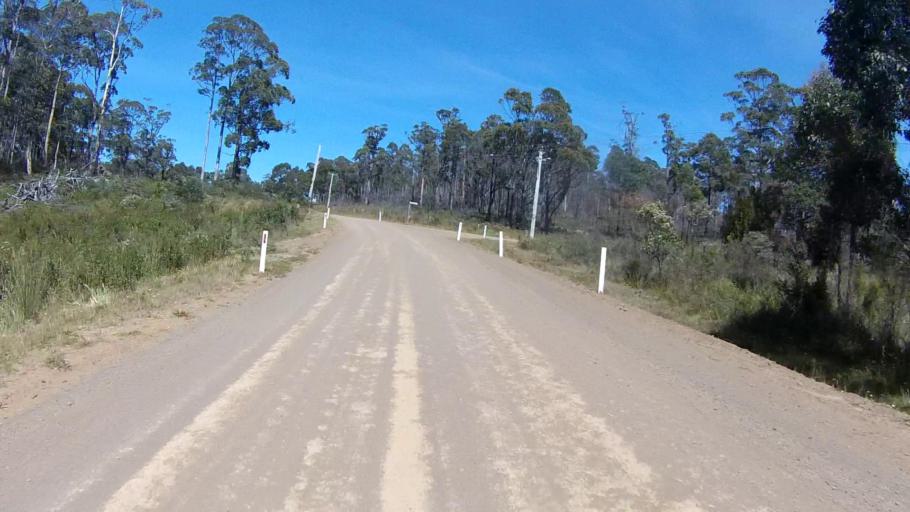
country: AU
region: Tasmania
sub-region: Sorell
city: Sorell
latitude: -42.7281
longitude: 147.7407
